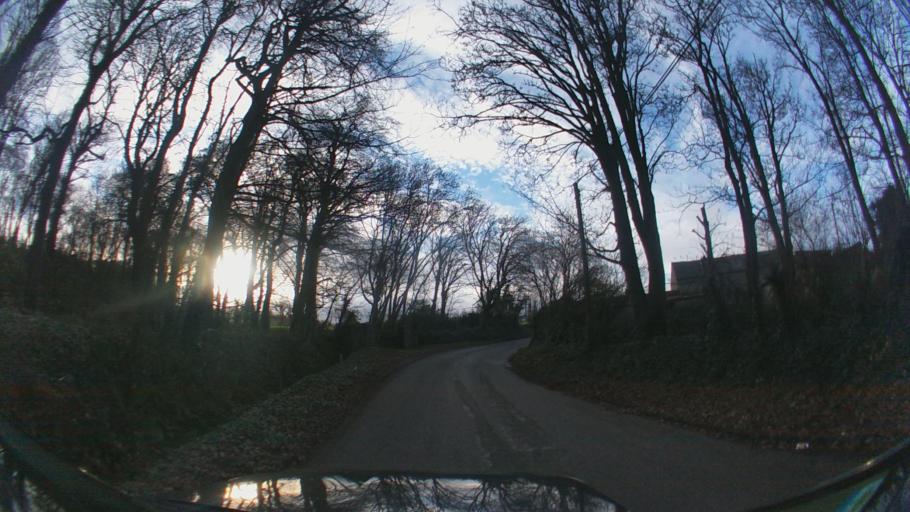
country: IE
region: Leinster
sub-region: Fingal County
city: Skerries
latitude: 53.5737
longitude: -6.1436
